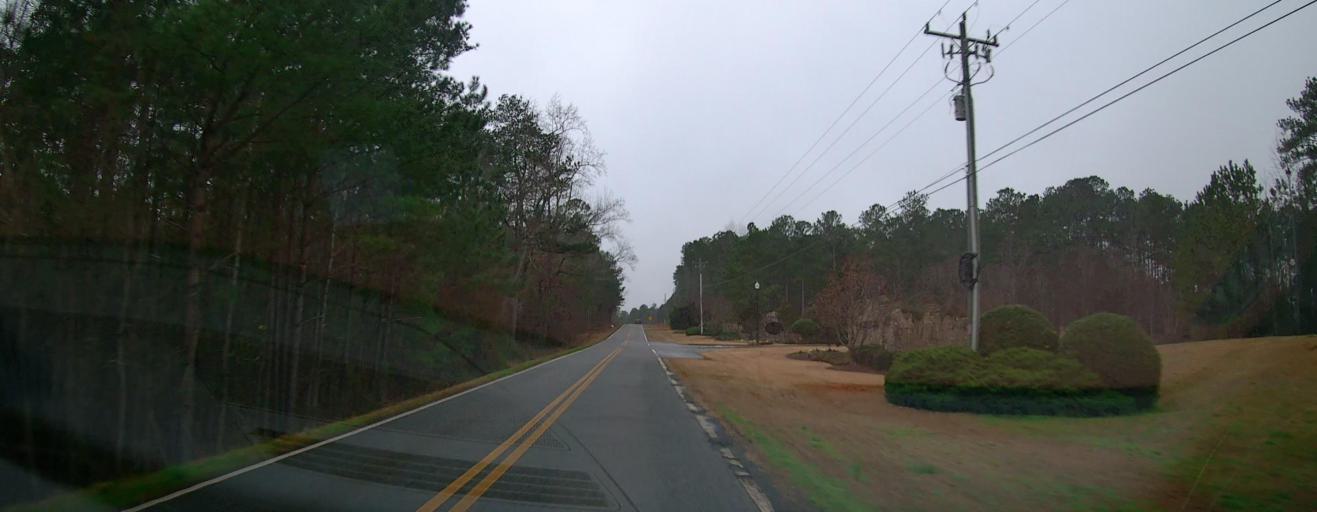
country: US
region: Georgia
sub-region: Monroe County
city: Forsyth
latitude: 33.1157
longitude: -83.9900
